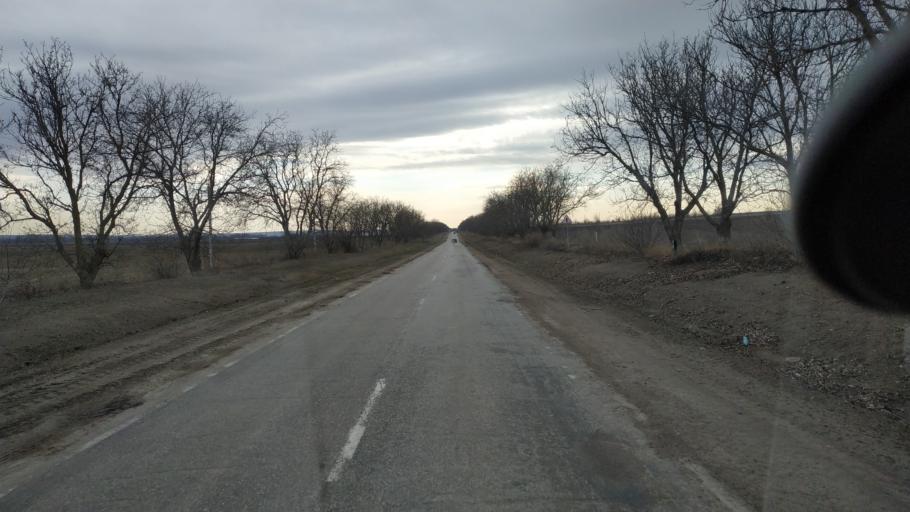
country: MD
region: Criuleni
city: Criuleni
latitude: 47.1887
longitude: 29.1440
